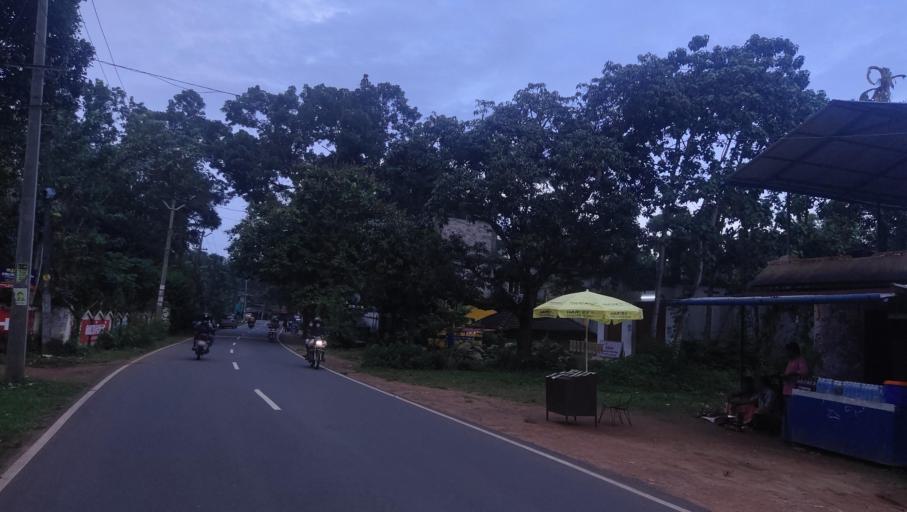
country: IN
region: Kerala
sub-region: Alappuzha
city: Kattanam
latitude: 9.1326
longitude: 76.6310
